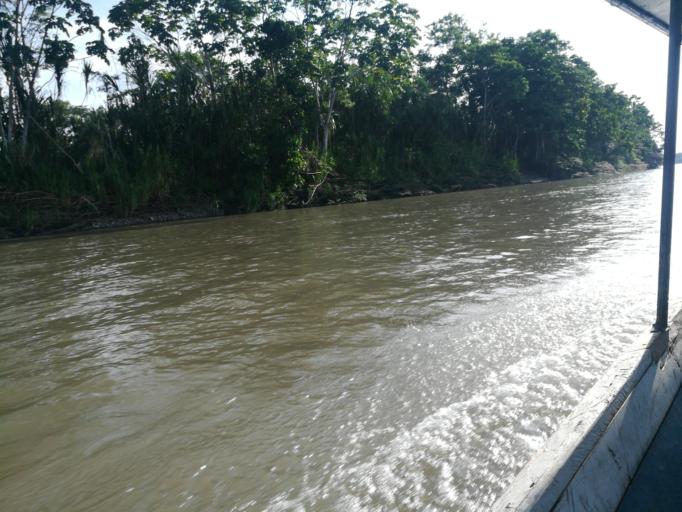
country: EC
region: Orellana
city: Boca Suno
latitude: -0.8509
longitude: -77.2351
